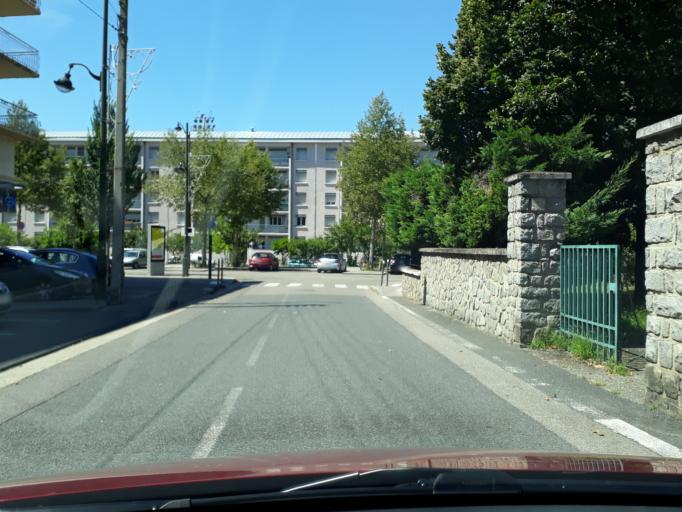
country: FR
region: Rhone-Alpes
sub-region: Departement du Rhone
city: Saint-Priest
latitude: 45.6955
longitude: 4.9421
